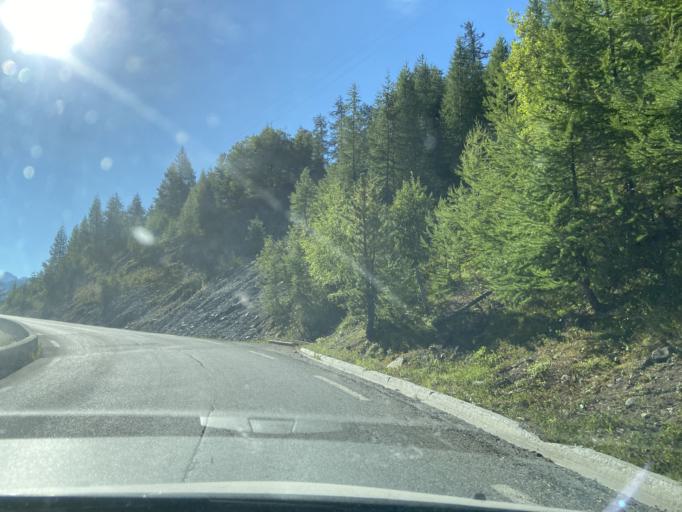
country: FR
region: Provence-Alpes-Cote d'Azur
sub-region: Departement des Hautes-Alpes
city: Guillestre
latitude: 44.6255
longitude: 6.6288
